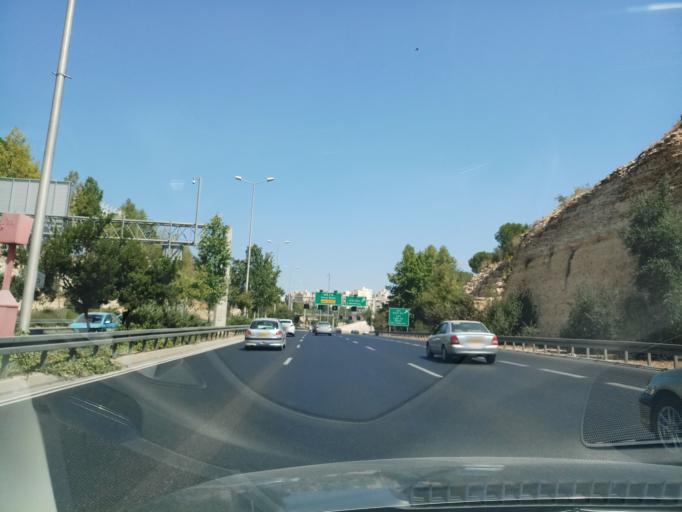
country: IL
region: Jerusalem
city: Jerusalem
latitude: 31.7621
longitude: 35.1937
